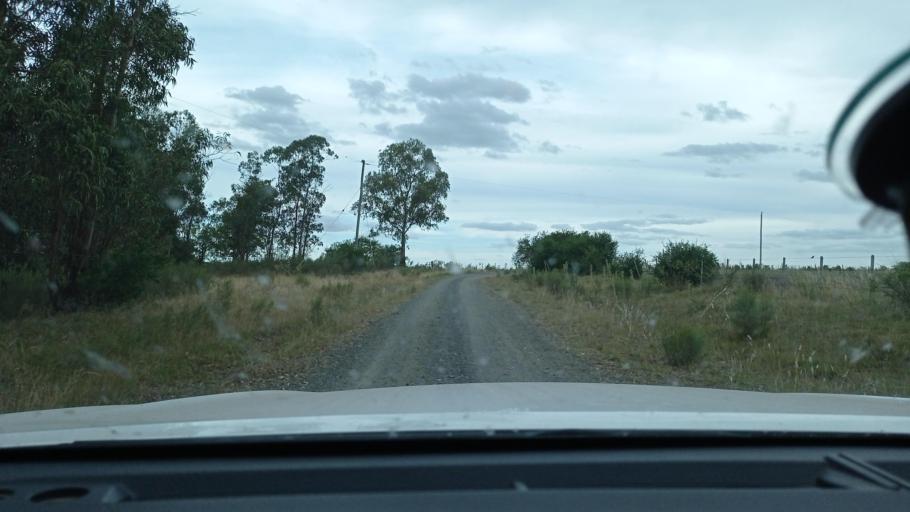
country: UY
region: Florida
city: Casupa
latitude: -34.1450
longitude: -55.7963
